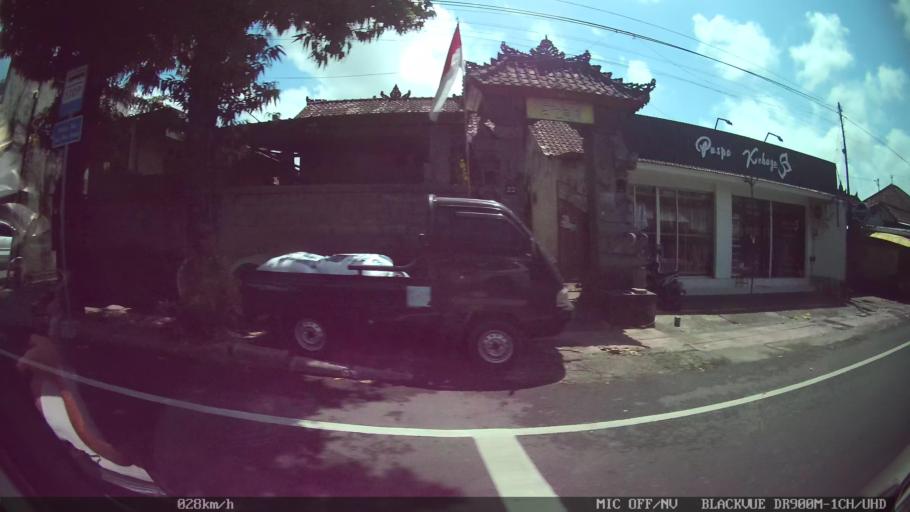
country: ID
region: Bali
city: Banjar Pasekan
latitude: -8.6030
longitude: 115.2800
